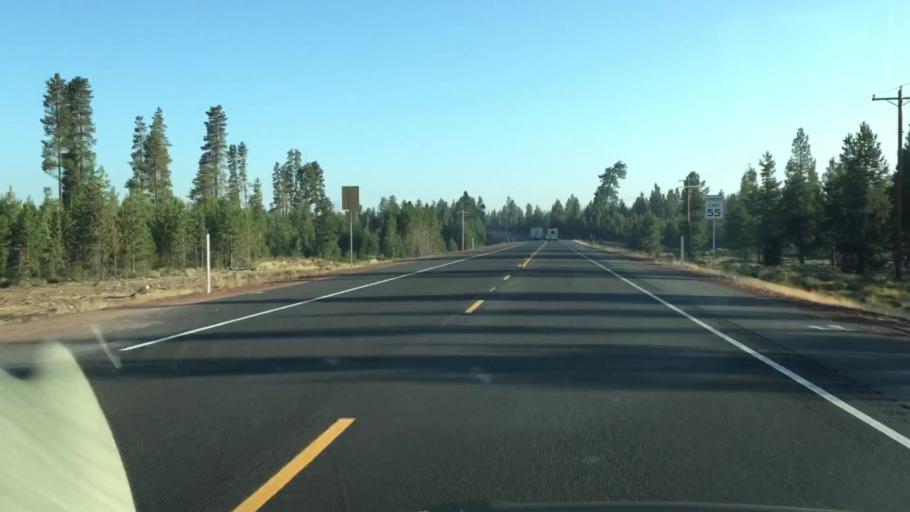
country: US
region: Oregon
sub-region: Deschutes County
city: La Pine
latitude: 43.2039
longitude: -121.7794
